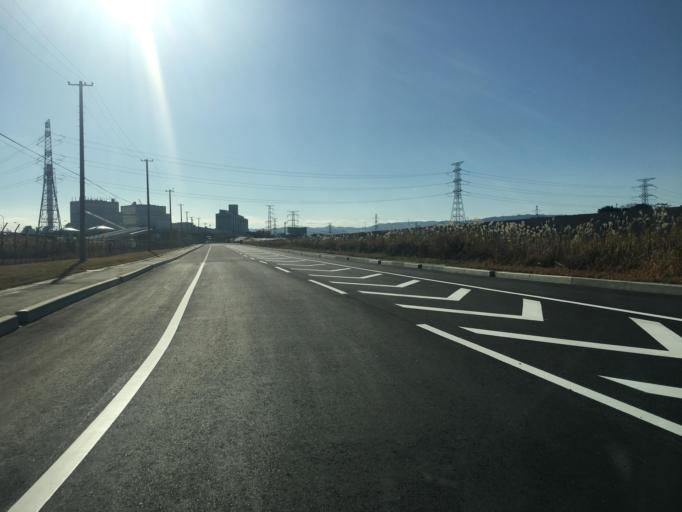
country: JP
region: Miyagi
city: Marumori
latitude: 37.8556
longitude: 140.9489
